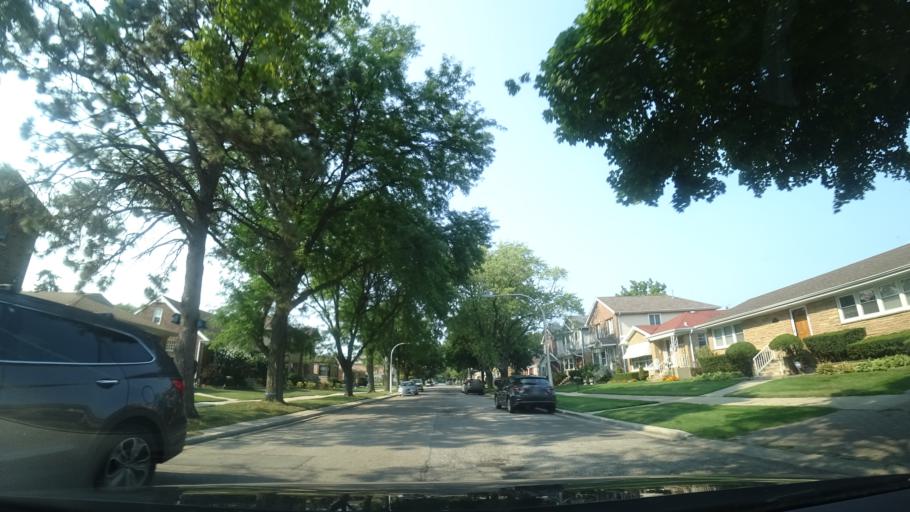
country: US
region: Illinois
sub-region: Cook County
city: Lincolnwood
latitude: 41.9944
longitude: -87.7349
